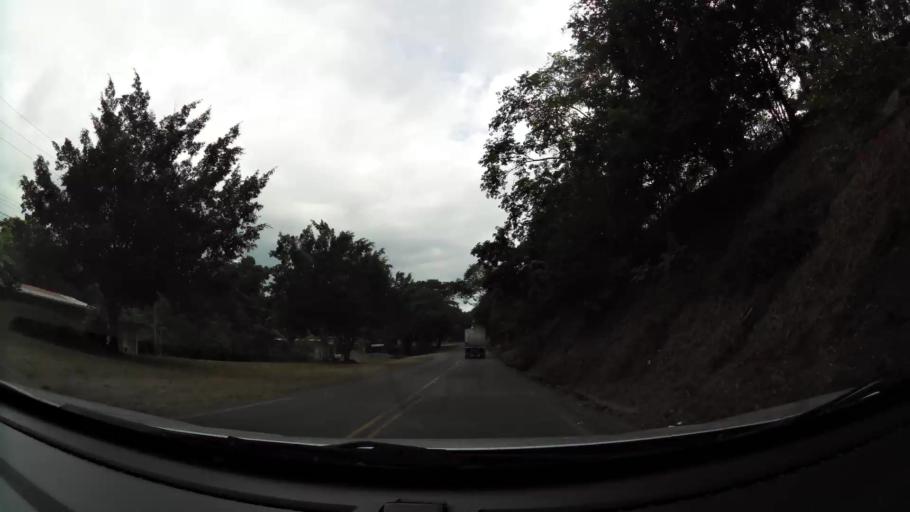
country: CR
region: Guanacaste
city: Juntas
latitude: 10.1617
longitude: -84.9178
